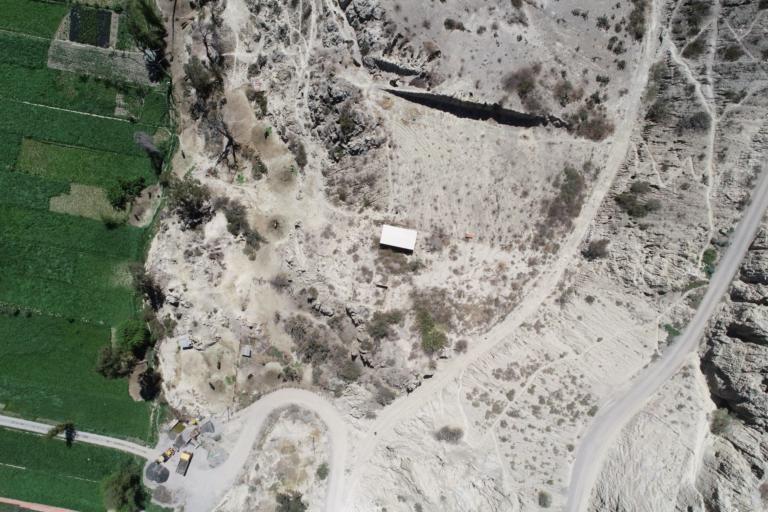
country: BO
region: La Paz
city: La Paz
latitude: -16.6317
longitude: -68.0556
